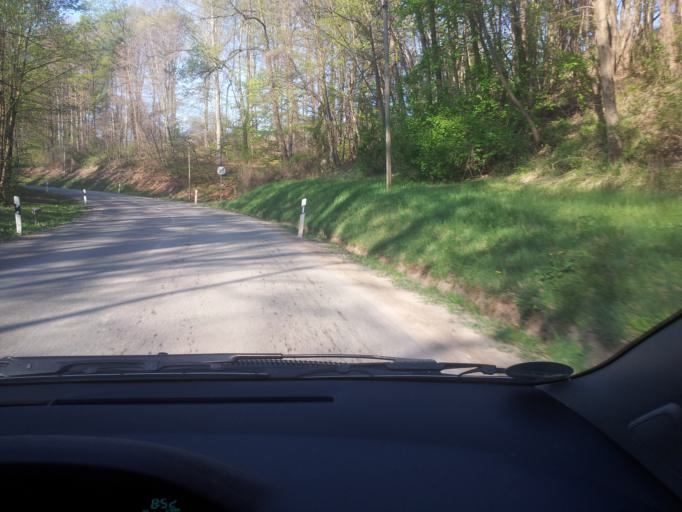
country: DE
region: Baden-Wuerttemberg
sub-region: Regierungsbezirk Stuttgart
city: Esslingen
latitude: 48.7727
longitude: 9.3240
